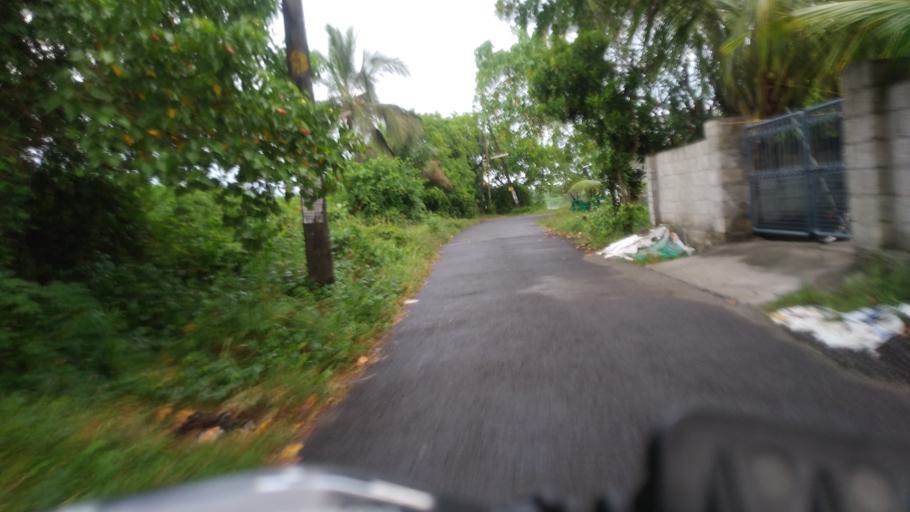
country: IN
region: Kerala
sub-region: Ernakulam
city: Elur
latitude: 10.0147
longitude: 76.2188
